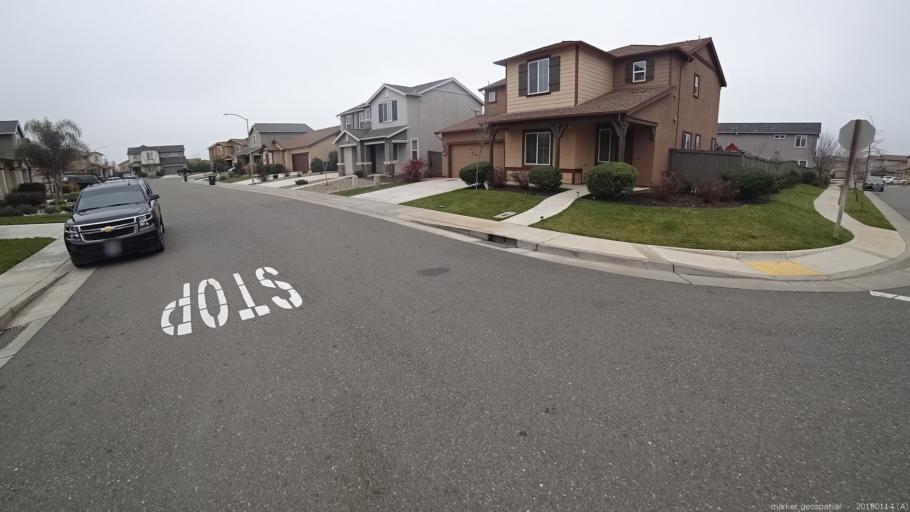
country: US
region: California
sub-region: Sacramento County
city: Rancho Cordova
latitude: 38.5299
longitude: -121.2291
